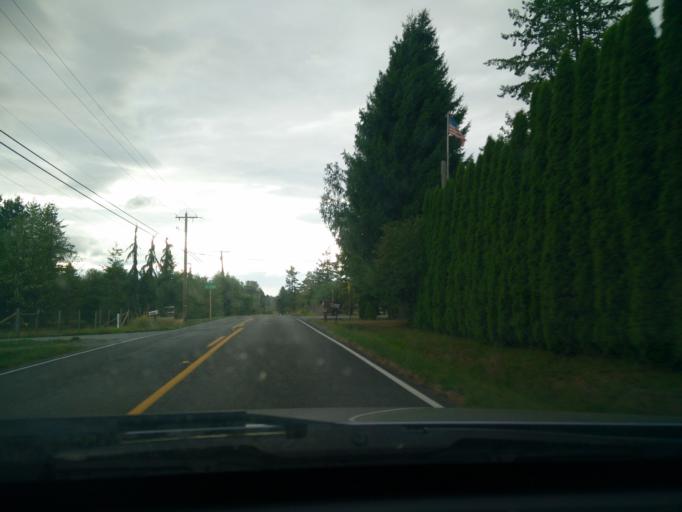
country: US
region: Washington
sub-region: Snohomish County
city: Stanwood
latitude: 48.2685
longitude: -122.3019
